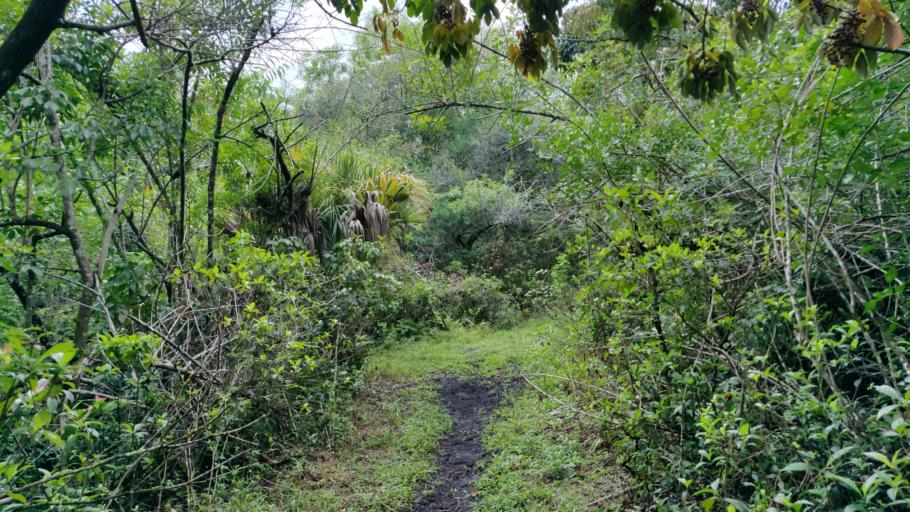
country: US
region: Florida
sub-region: Broward County
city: Cooper City
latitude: 26.0755
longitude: -80.2725
